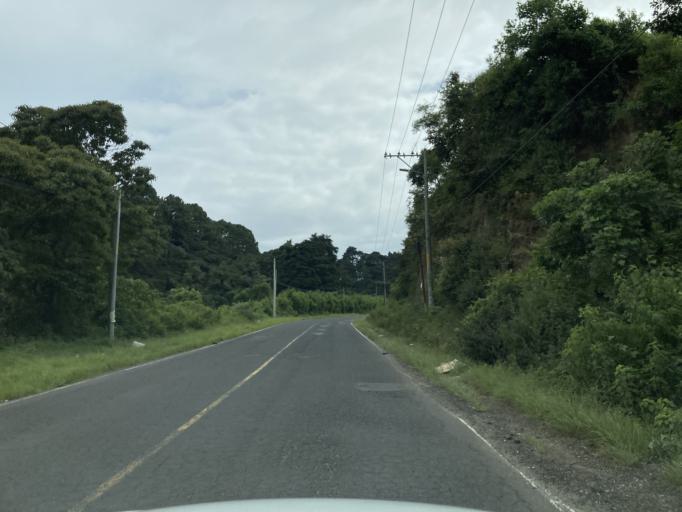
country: GT
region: Guatemala
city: San Jose Pinula
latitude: 14.5317
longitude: -90.4098
